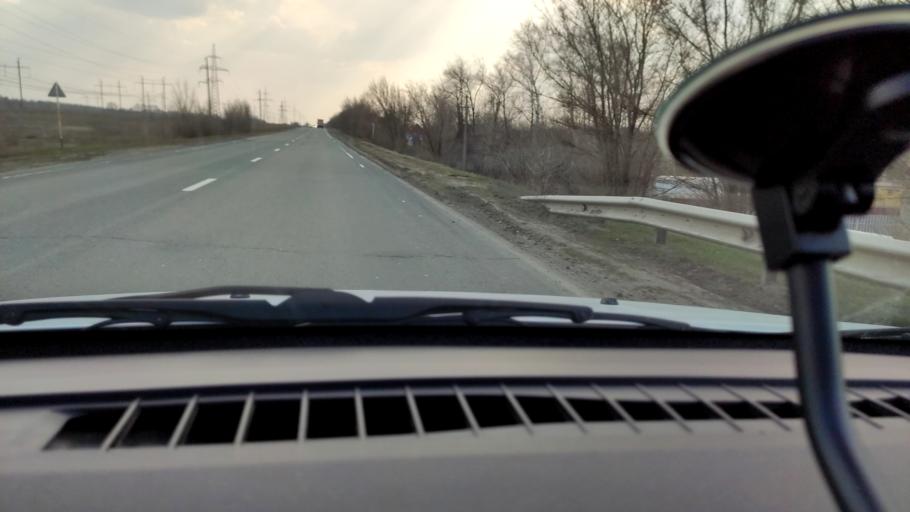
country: RU
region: Samara
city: Smyshlyayevka
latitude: 53.0890
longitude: 50.3962
